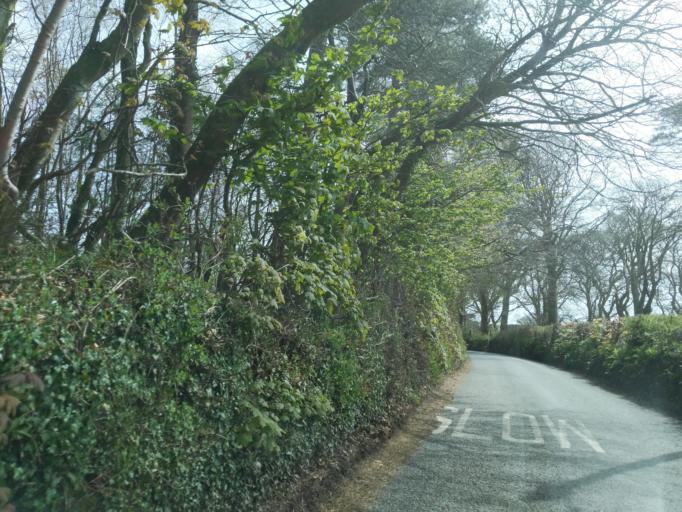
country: GB
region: England
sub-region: Devon
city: Yealmpton
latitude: 50.4005
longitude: -4.0066
